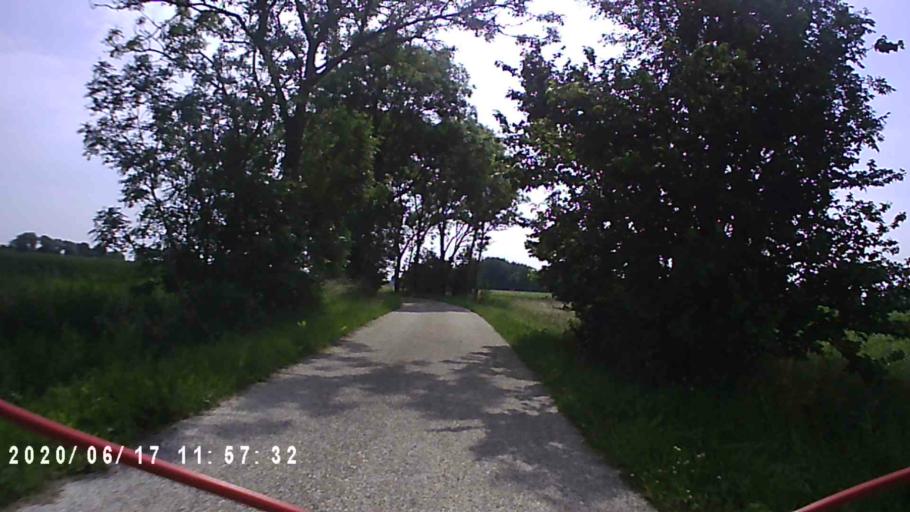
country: NL
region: Groningen
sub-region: Gemeente De Marne
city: Ulrum
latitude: 53.3462
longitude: 6.3245
